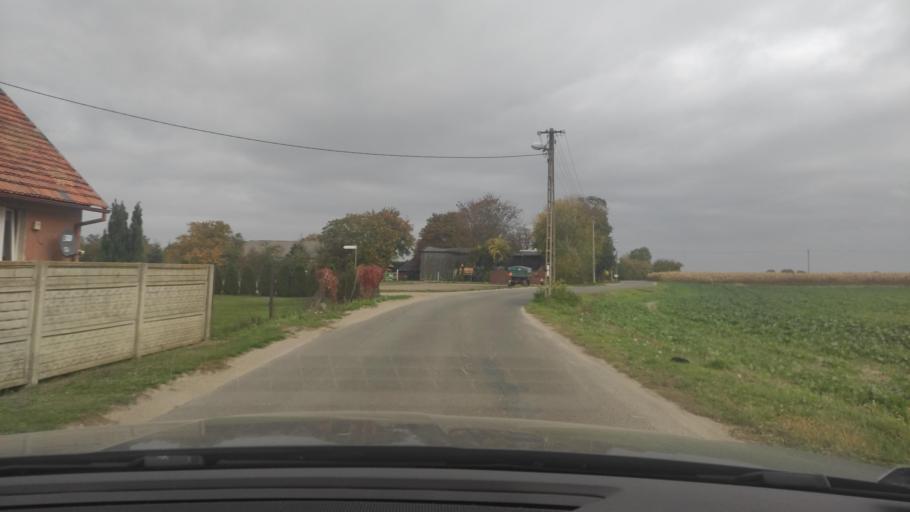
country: PL
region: Greater Poland Voivodeship
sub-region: Powiat poznanski
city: Kostrzyn
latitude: 52.4462
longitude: 17.2084
